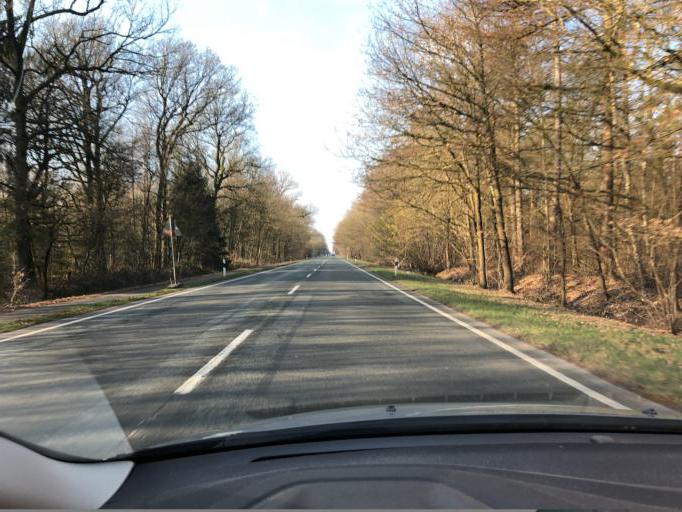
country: DE
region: Lower Saxony
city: Firrel
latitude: 53.3069
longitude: 7.6440
